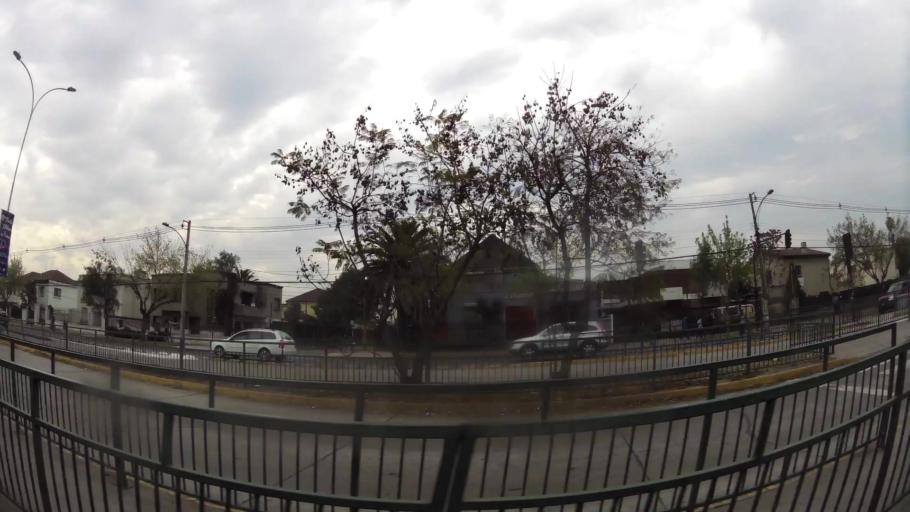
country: CL
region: Santiago Metropolitan
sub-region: Provincia de Santiago
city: Villa Presidente Frei, Nunoa, Santiago, Chile
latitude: -33.4620
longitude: -70.6129
